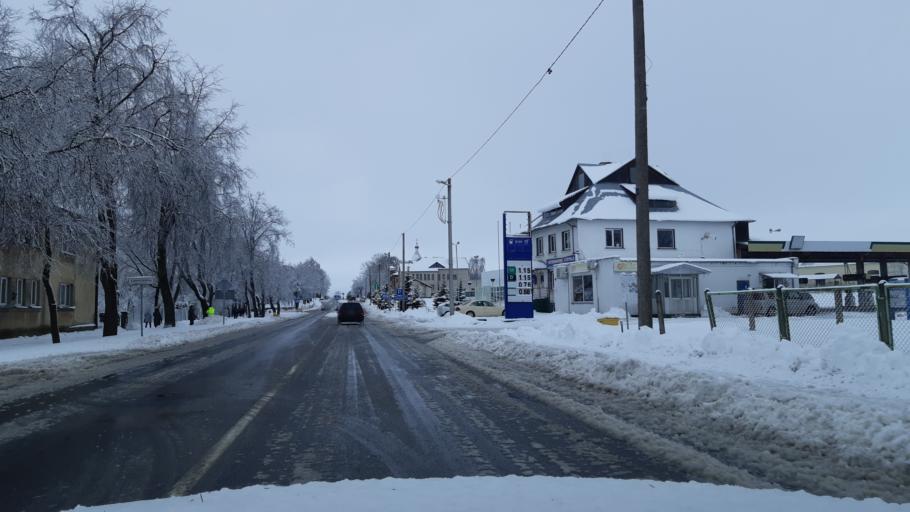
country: LT
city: Kybartai
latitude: 54.6381
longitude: 22.7641
